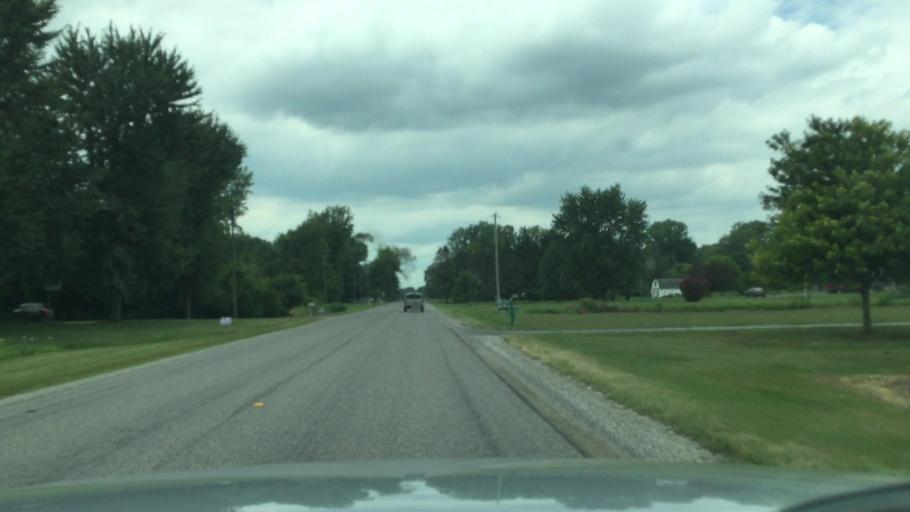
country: US
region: Michigan
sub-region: Saginaw County
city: Birch Run
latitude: 43.2502
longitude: -83.8051
